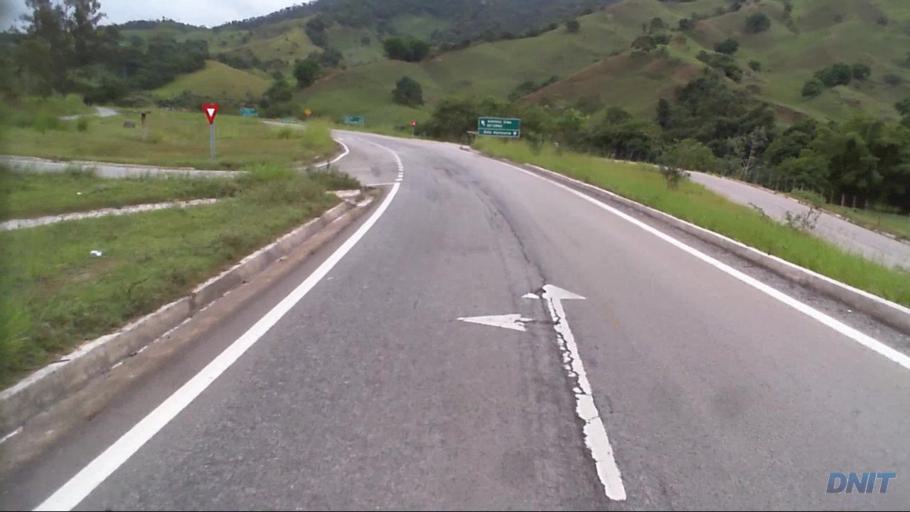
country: BR
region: Minas Gerais
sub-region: Timoteo
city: Timoteo
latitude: -19.6177
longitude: -42.8486
